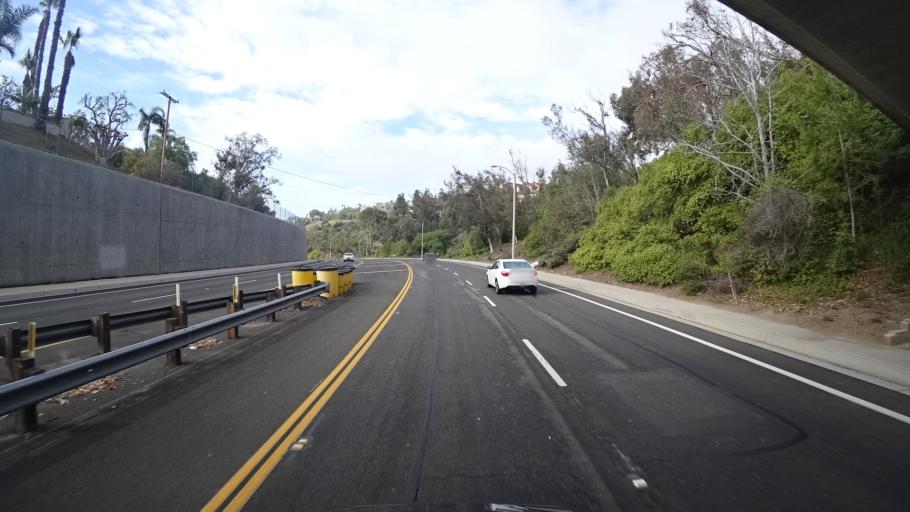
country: US
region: California
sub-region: Orange County
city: North Tustin
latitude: 33.7816
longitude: -117.7751
